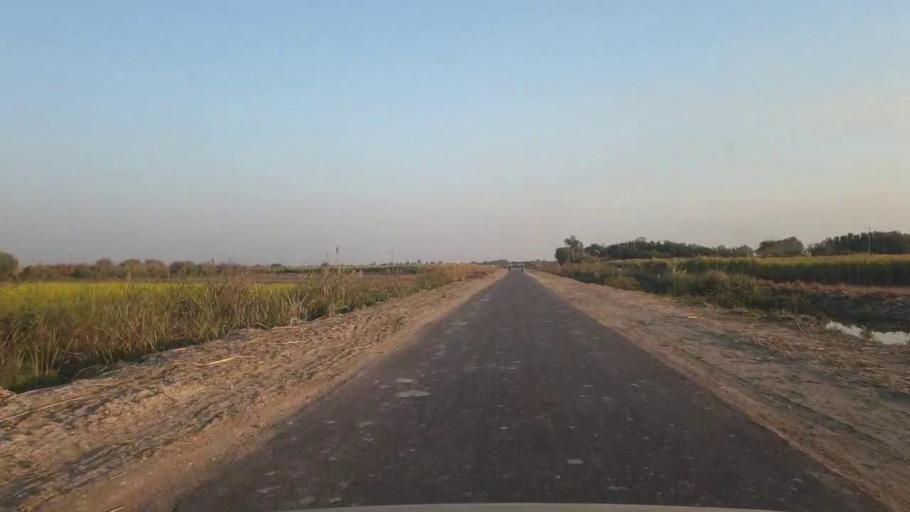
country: PK
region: Sindh
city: Chambar
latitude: 25.2800
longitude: 68.9135
